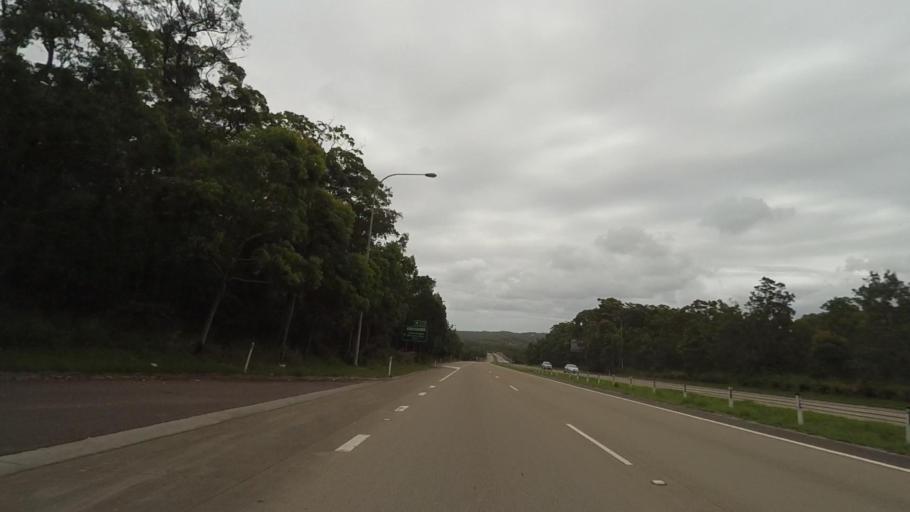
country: AU
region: New South Wales
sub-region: Lake Macquarie Shire
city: Kotara
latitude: -32.9530
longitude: 151.6825
